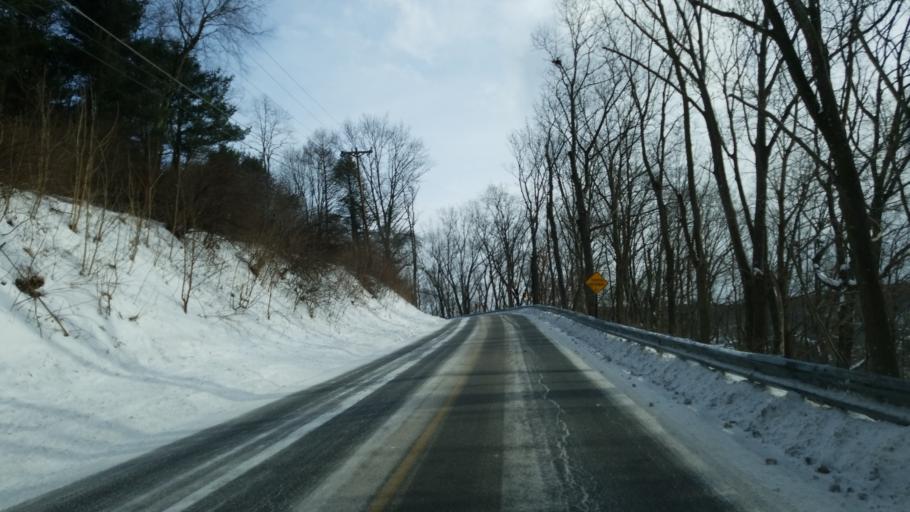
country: US
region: Pennsylvania
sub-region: Clearfield County
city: Clearfield
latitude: 41.0157
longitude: -78.4479
